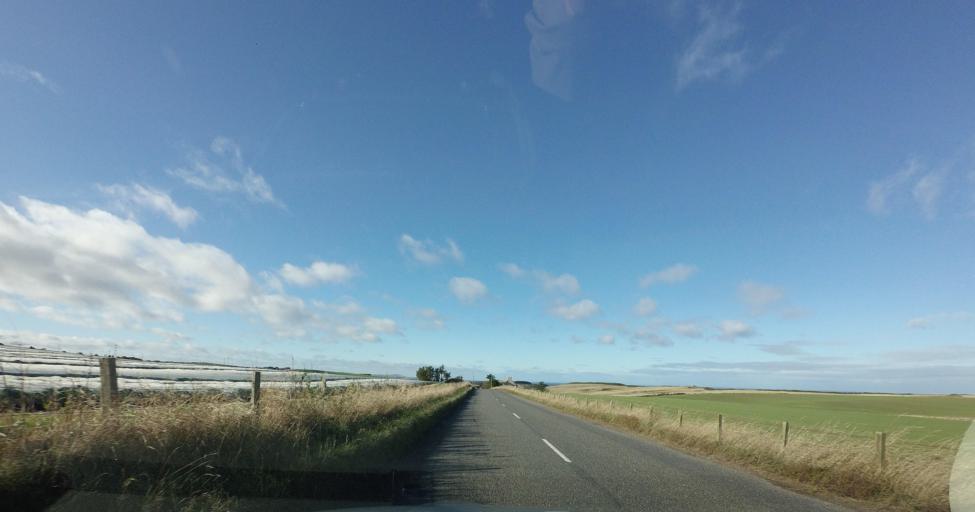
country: GB
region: Scotland
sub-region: Aberdeenshire
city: Macduff
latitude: 57.6633
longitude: -2.3790
